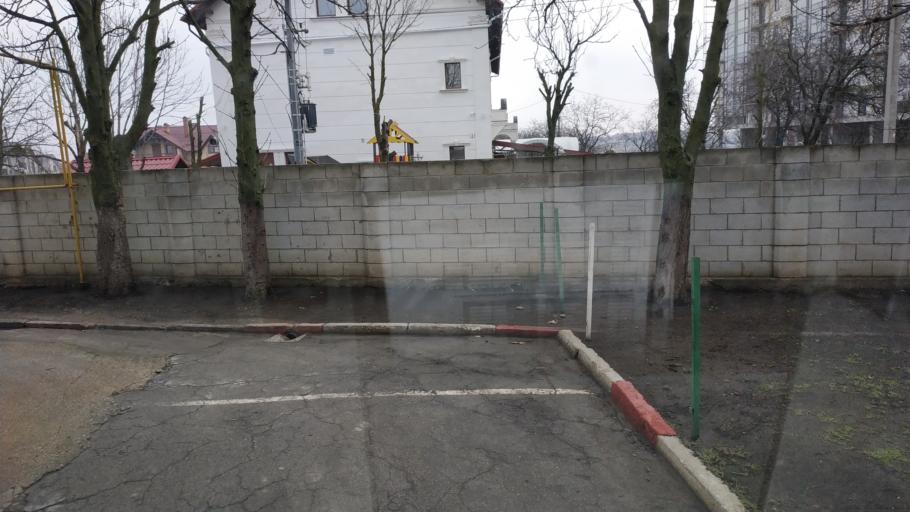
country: MD
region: Chisinau
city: Vatra
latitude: 47.0145
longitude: 28.7518
